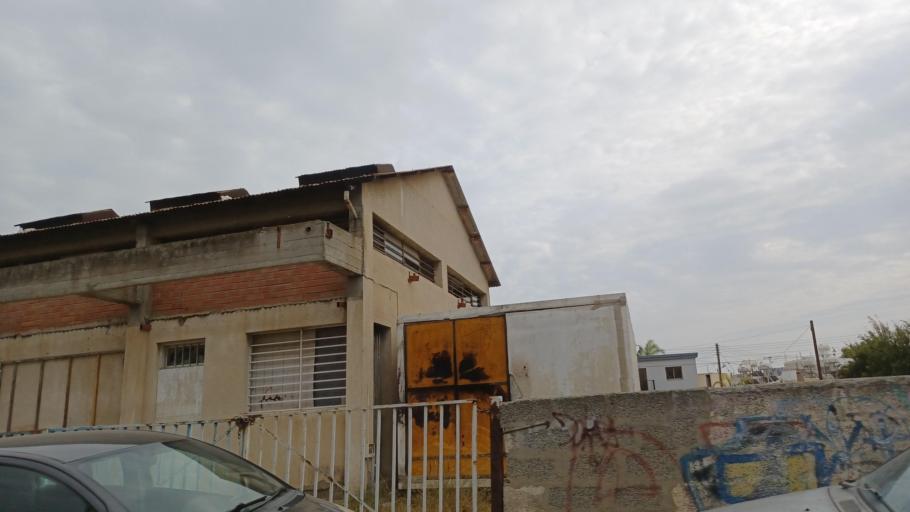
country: CY
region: Limassol
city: Limassol
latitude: 34.6699
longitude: 33.0048
